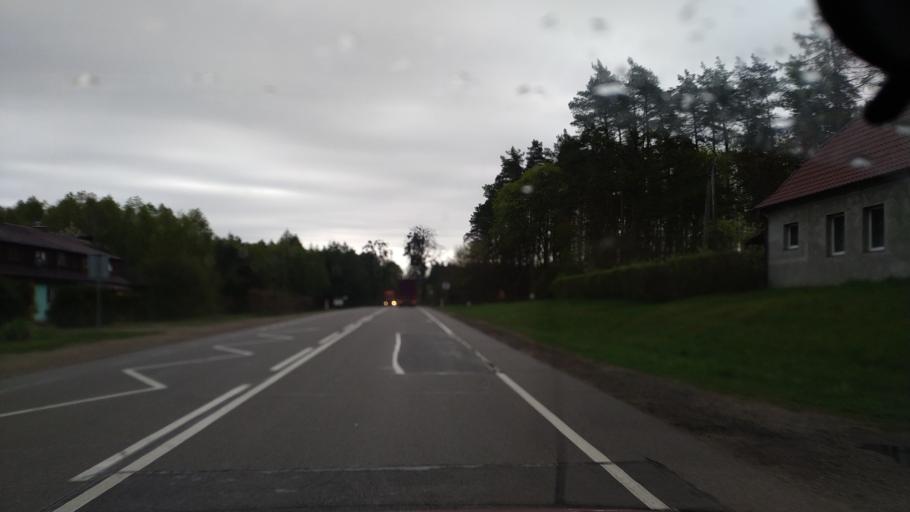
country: PL
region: Pomeranian Voivodeship
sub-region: Powiat starogardzki
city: Kaliska
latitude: 53.8772
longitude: 18.1802
